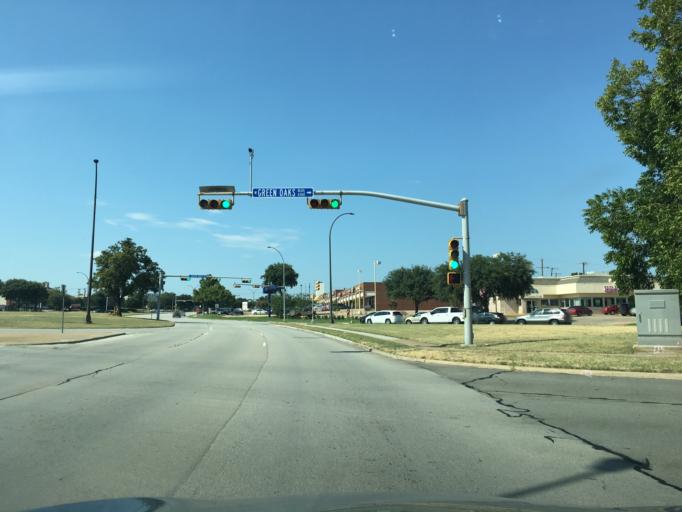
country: US
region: Texas
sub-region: Tarrant County
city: Kennedale
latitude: 32.6788
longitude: -97.1959
